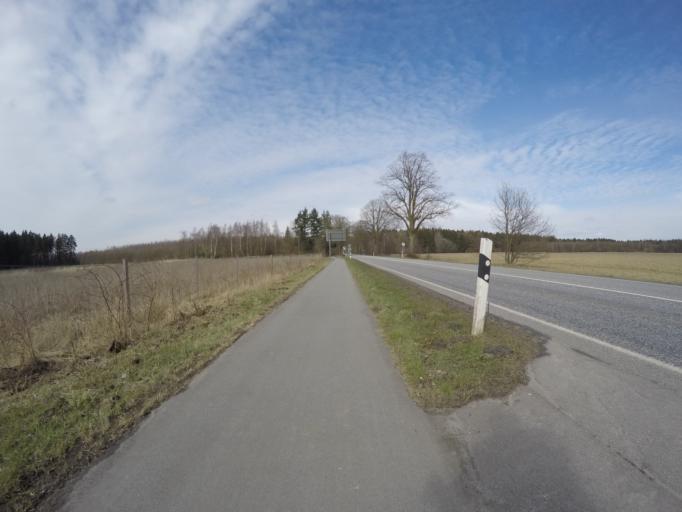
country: DE
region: Schleswig-Holstein
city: Langeln
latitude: 53.8138
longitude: 9.8804
